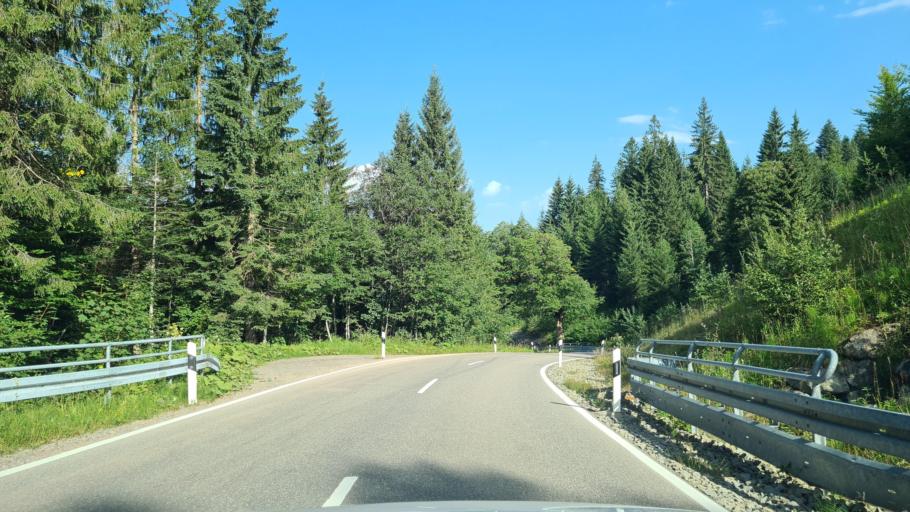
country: DE
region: Bavaria
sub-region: Swabia
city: Balderschwang
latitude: 47.4374
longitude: 10.1455
